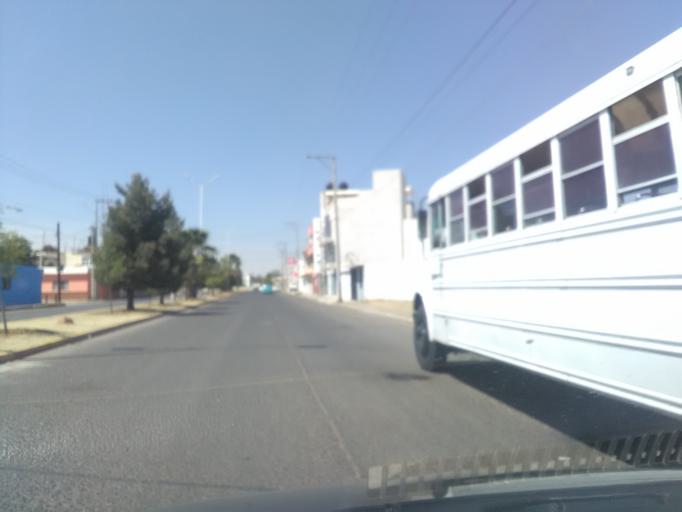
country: MX
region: Durango
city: Victoria de Durango
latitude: 24.0397
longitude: -104.6501
